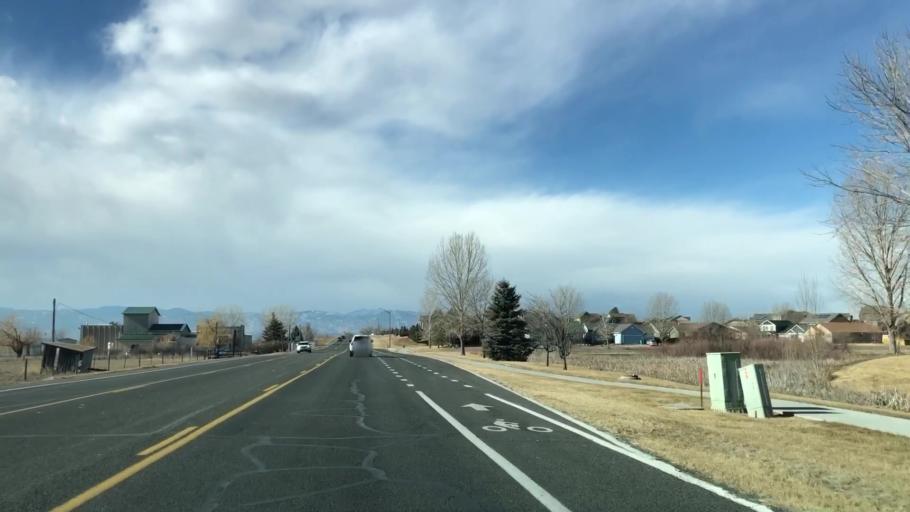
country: US
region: Colorado
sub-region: Larimer County
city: Fort Collins
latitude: 40.5957
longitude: -105.0068
